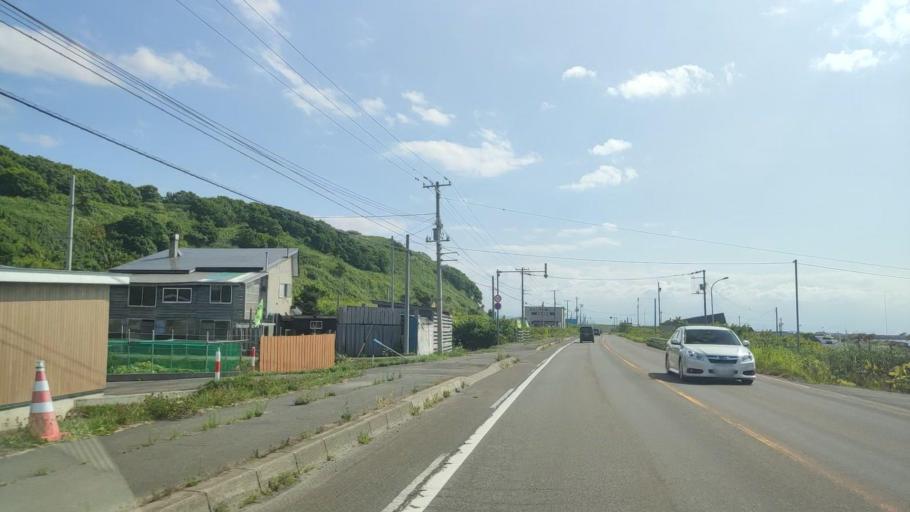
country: JP
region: Hokkaido
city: Rumoi
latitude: 43.9829
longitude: 141.6477
